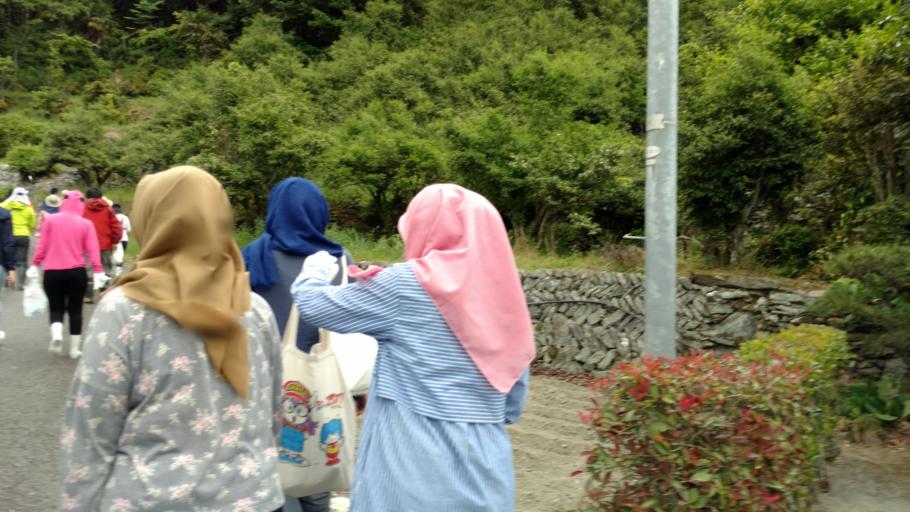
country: JP
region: Ehime
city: Saijo
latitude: 33.8644
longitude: 133.1984
